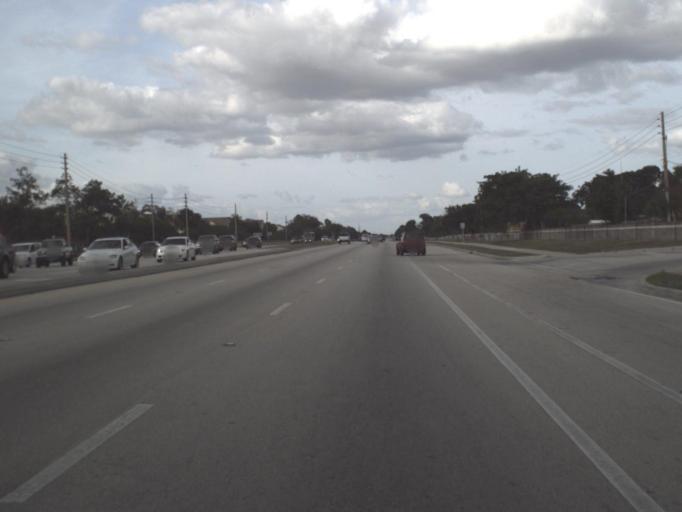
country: US
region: Florida
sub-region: Orange County
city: Oak Ridge
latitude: 28.4728
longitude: -81.4174
